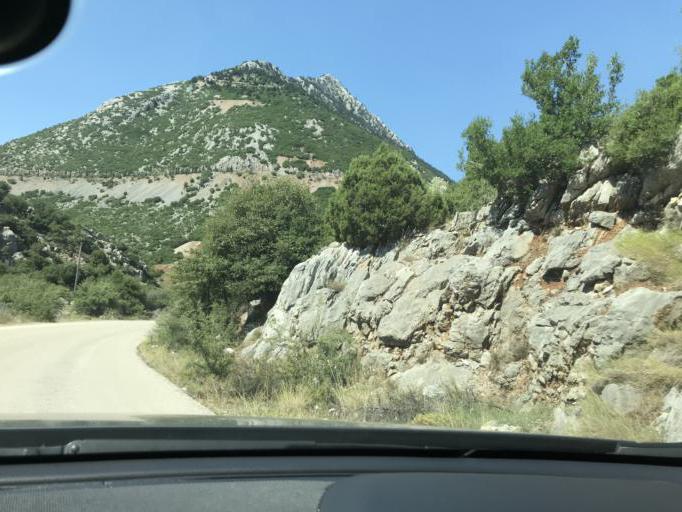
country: GR
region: Central Greece
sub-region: Nomos Voiotias
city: Distomo
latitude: 38.4760
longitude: 22.6838
